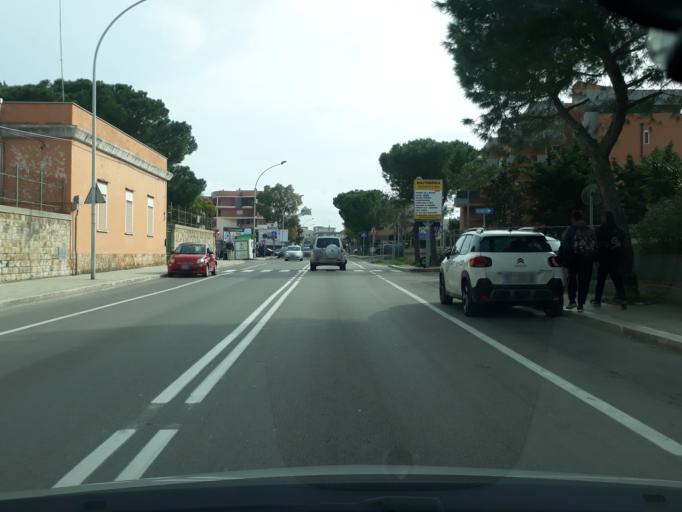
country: IT
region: Apulia
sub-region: Provincia di Bari
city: Monopoli
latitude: 40.9502
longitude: 17.2884
